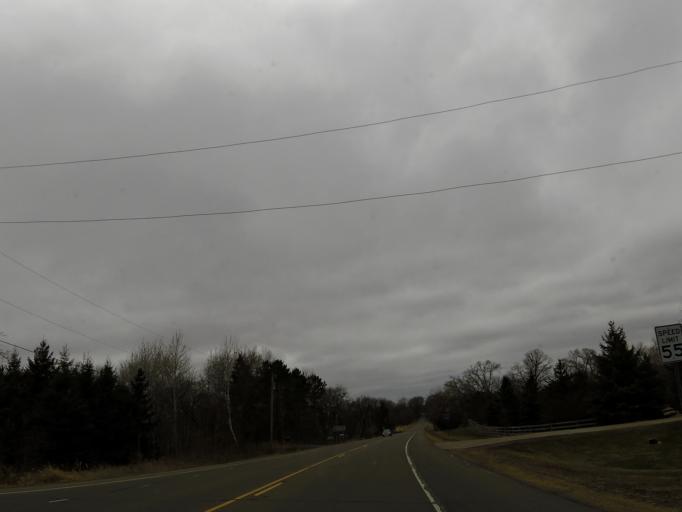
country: US
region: Minnesota
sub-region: Washington County
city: Oak Park Heights
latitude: 45.0072
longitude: -92.8234
